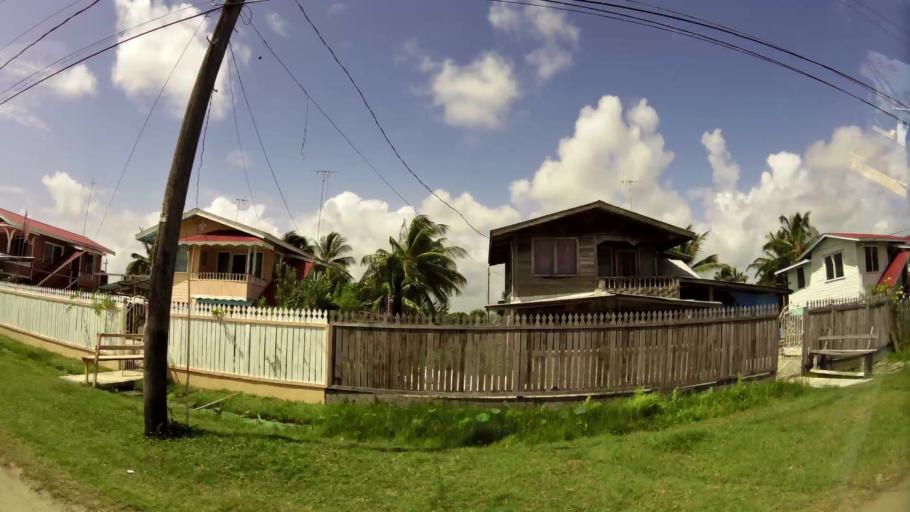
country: GY
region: Demerara-Mahaica
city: Mahaica Village
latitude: 6.7685
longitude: -58.0056
